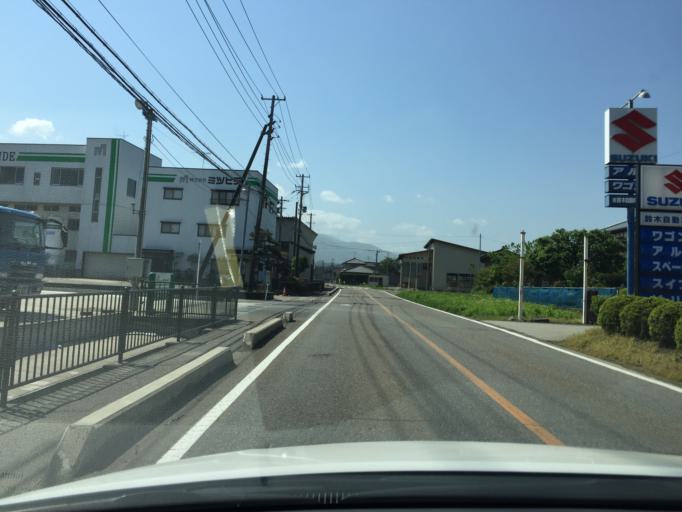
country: JP
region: Niigata
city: Muramatsu
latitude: 37.6865
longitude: 139.1515
